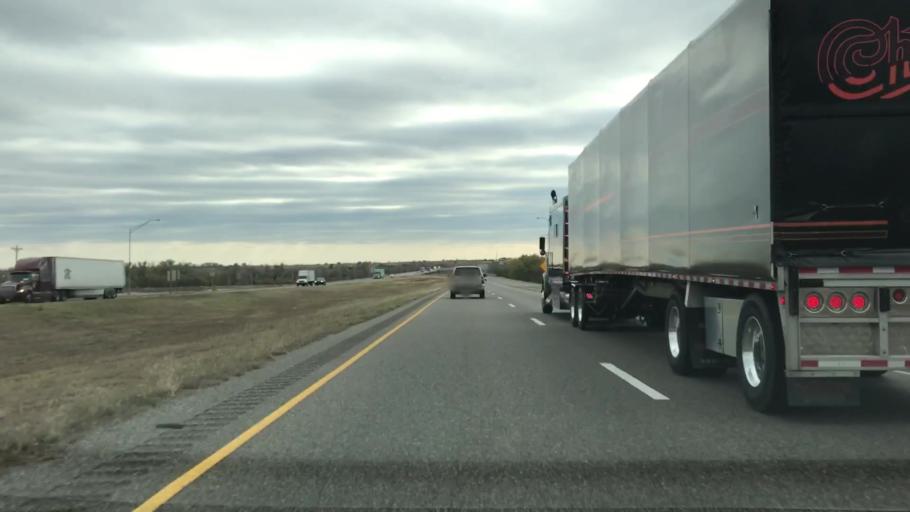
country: US
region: Oklahoma
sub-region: Beckham County
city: Sayre
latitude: 35.2909
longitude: -99.6206
